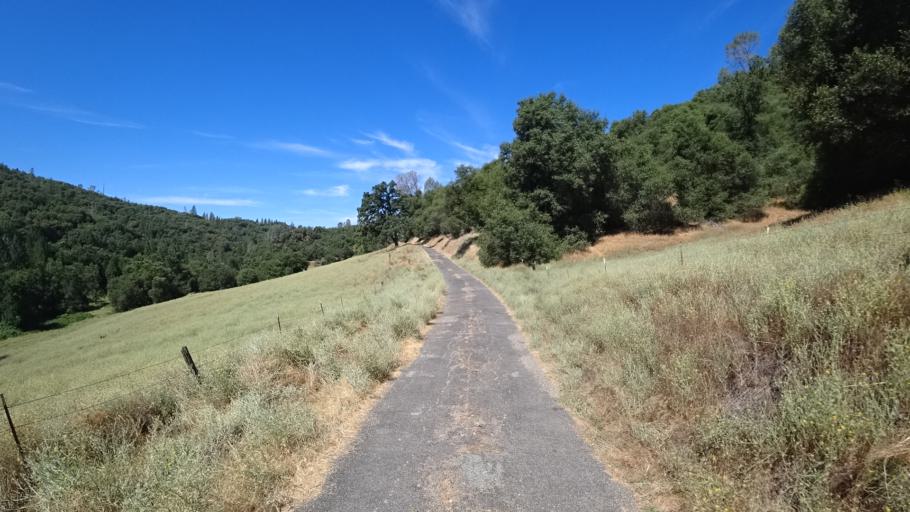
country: US
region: California
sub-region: Calaveras County
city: Murphys
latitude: 38.1437
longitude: -120.5273
